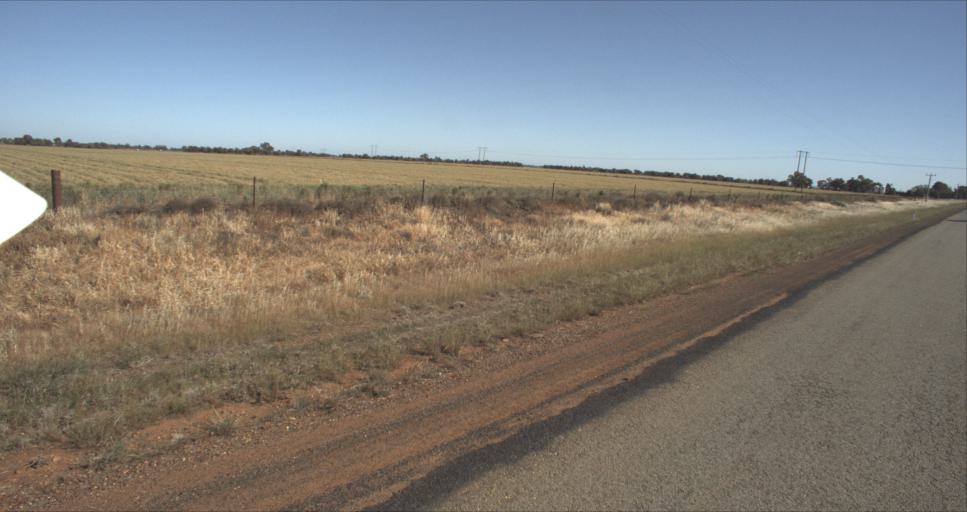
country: AU
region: New South Wales
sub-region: Leeton
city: Leeton
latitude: -34.5618
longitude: 146.2652
